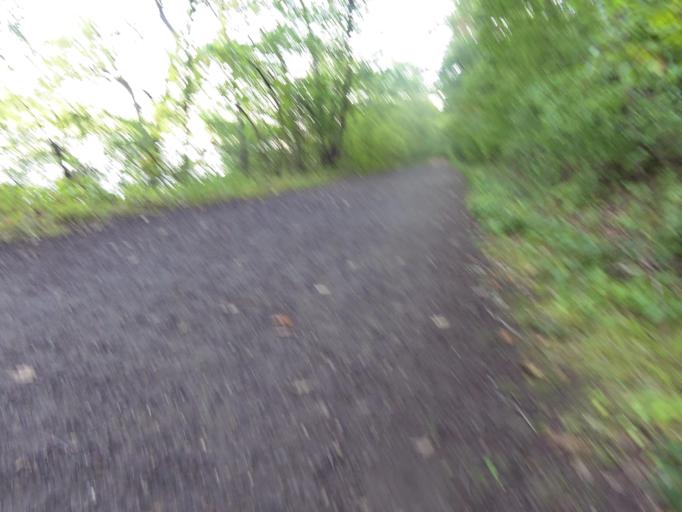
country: US
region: Minnesota
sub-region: Washington County
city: Afton
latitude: 44.8560
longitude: -92.7729
